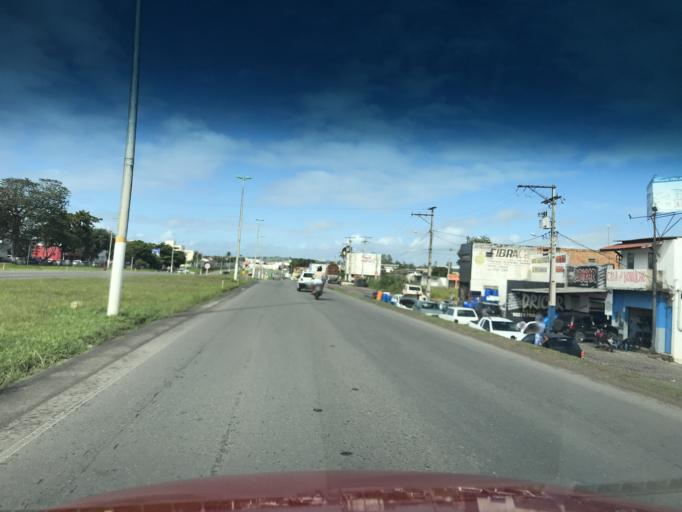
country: BR
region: Bahia
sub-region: Santo Antonio De Jesus
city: Santo Antonio de Jesus
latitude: -12.9651
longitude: -39.2725
